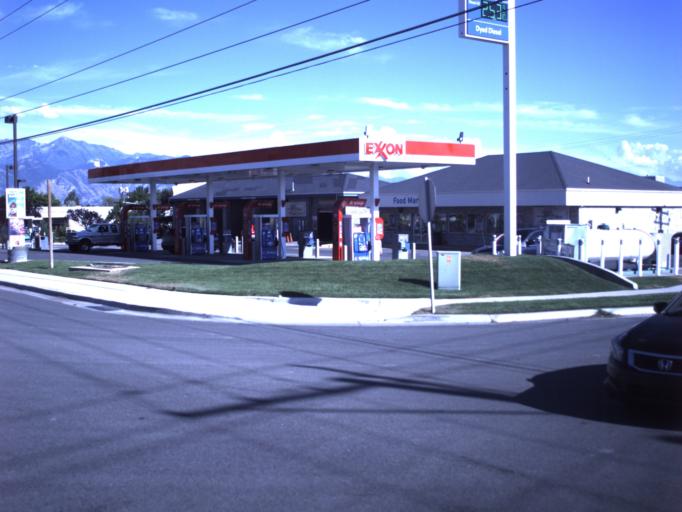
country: US
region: Utah
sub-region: Utah County
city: American Fork
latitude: 40.3713
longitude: -111.7744
